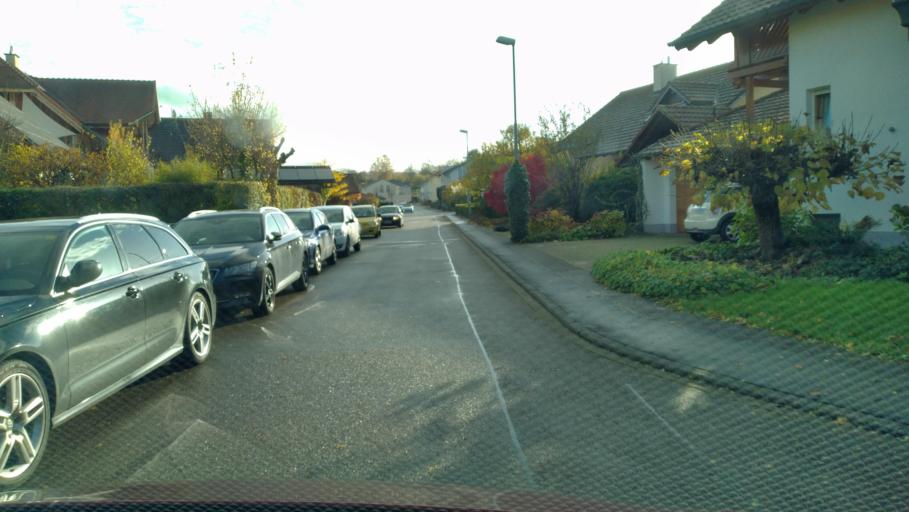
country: DE
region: Baden-Wuerttemberg
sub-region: Freiburg Region
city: Malterdingen
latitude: 48.1602
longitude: 7.8003
